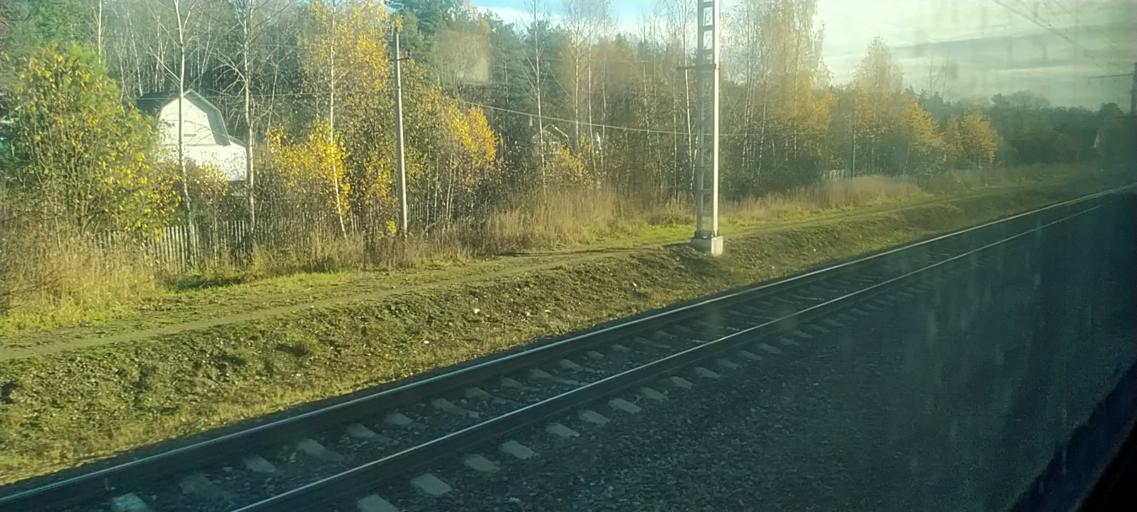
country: RU
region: Moskovskaya
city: Ramenskoye
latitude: 55.6368
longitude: 38.2709
